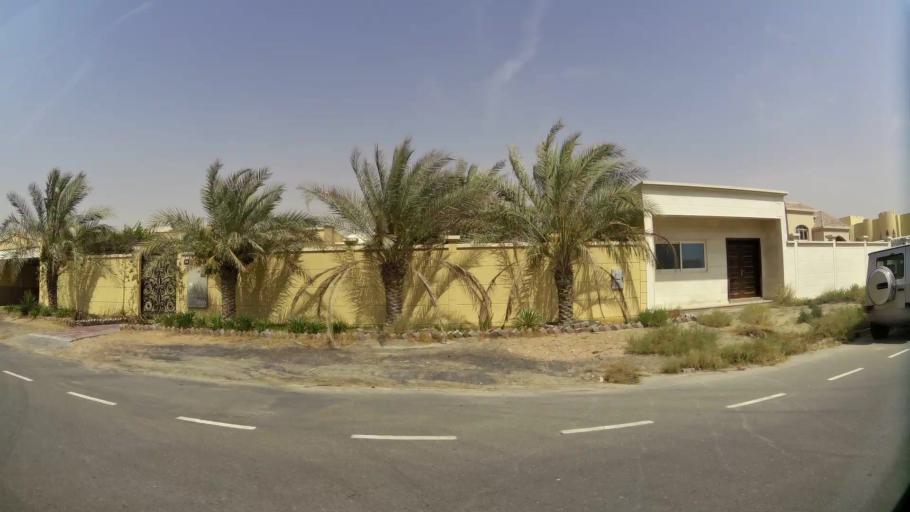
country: AE
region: Ash Shariqah
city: Sharjah
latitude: 25.2531
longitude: 55.4776
